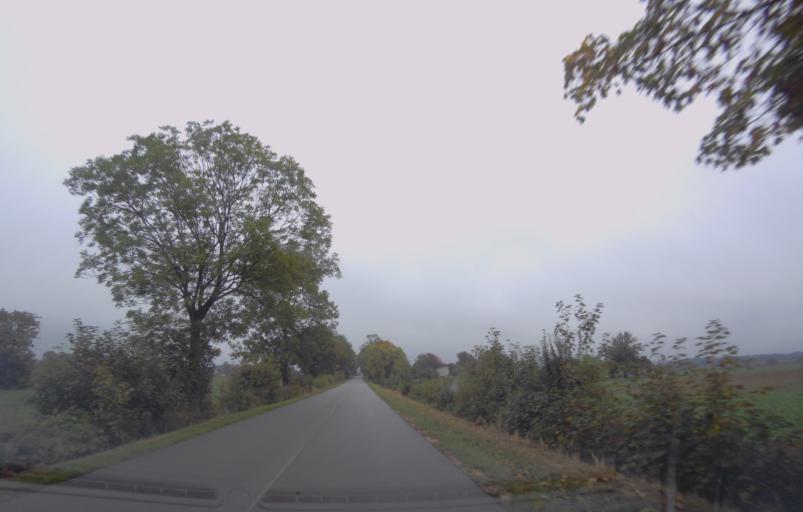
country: PL
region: Lublin Voivodeship
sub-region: Powiat chelmski
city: Sawin
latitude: 51.2140
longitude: 23.4465
